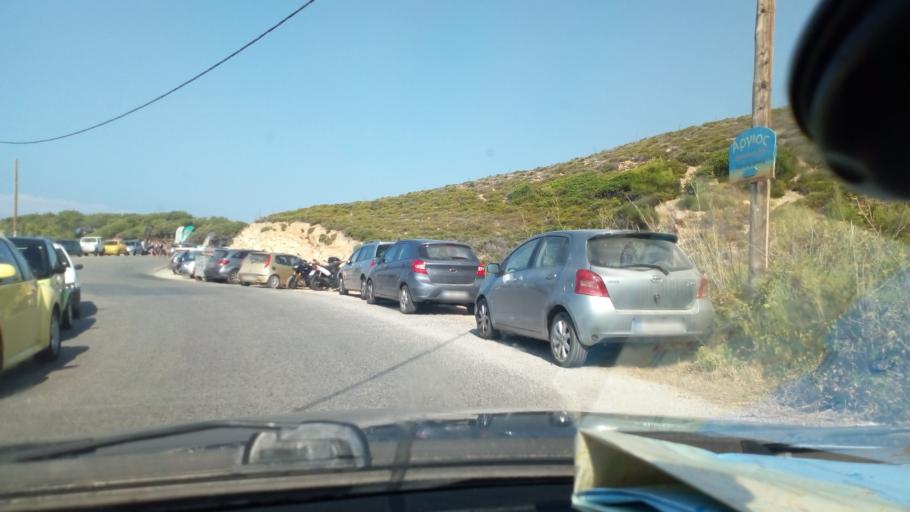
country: GR
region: North Aegean
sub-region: Nomos Samou
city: Agios Kirykos
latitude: 37.6296
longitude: 26.0971
